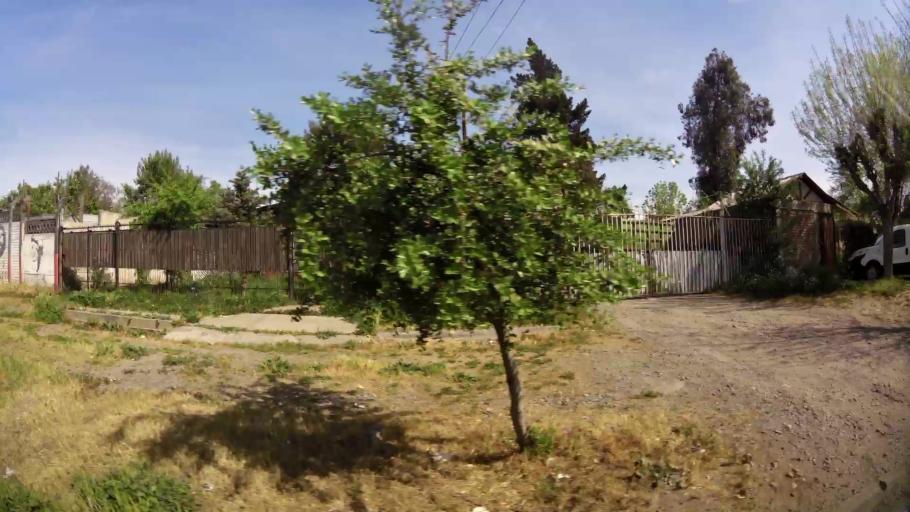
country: CL
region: Santiago Metropolitan
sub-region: Provincia de Santiago
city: La Pintana
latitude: -33.5416
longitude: -70.6302
